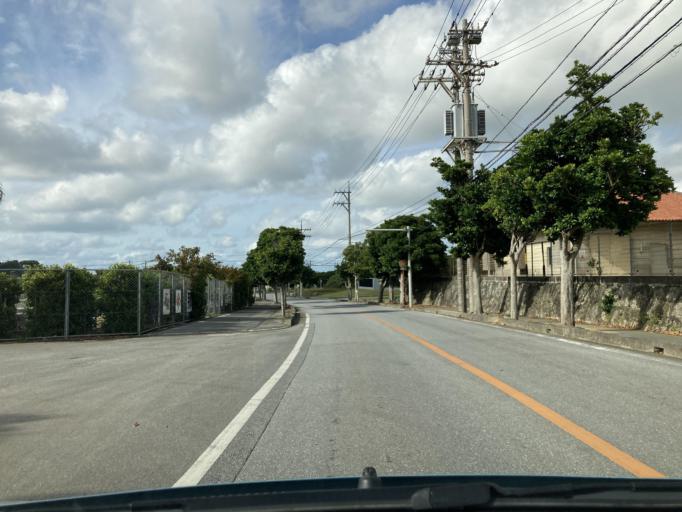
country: JP
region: Okinawa
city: Itoman
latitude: 26.1216
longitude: 127.7147
